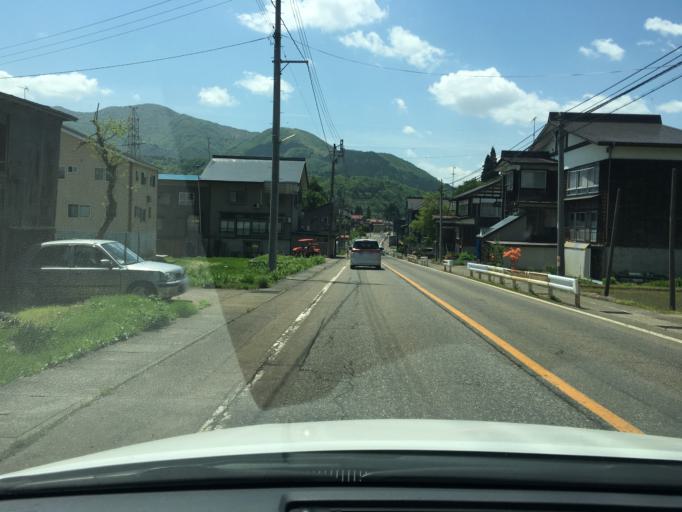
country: JP
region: Niigata
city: Tochio-honcho
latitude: 37.3153
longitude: 139.0142
